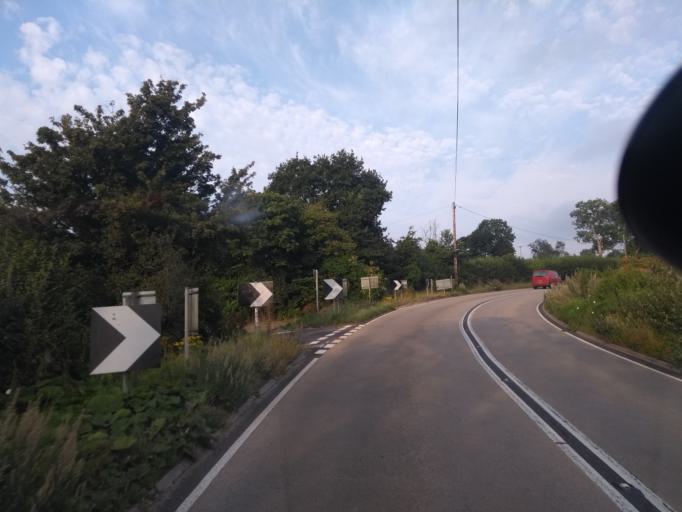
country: GB
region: England
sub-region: Somerset
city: Chard
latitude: 50.9160
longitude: -3.0019
